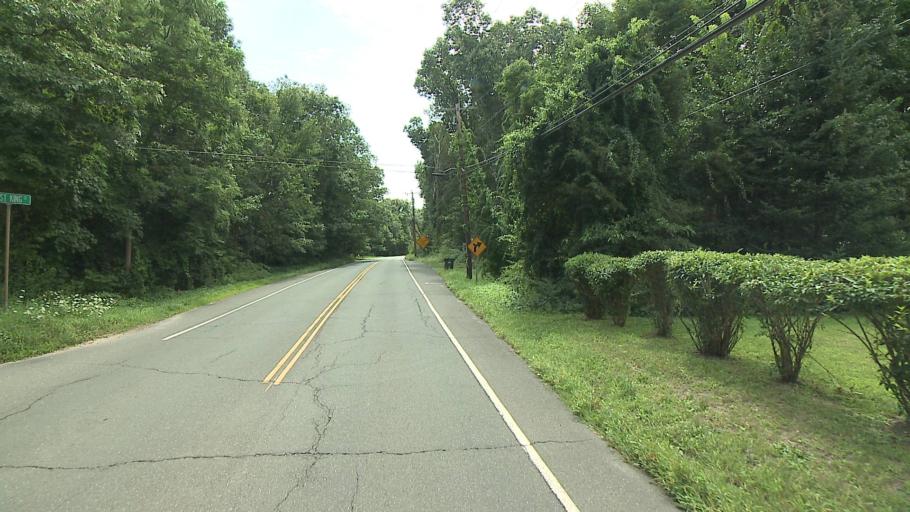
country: US
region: New York
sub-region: Putnam County
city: Putnam Lake
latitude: 41.4408
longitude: -73.5006
